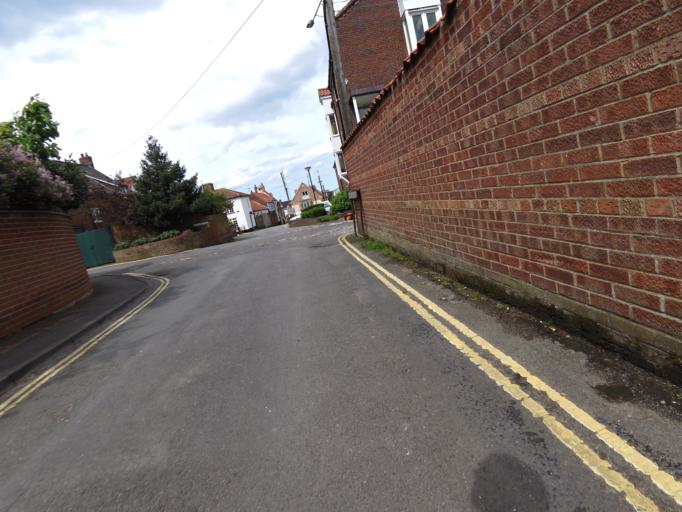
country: GB
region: England
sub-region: Norfolk
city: Wells-next-the-Sea
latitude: 52.9560
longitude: 0.8515
